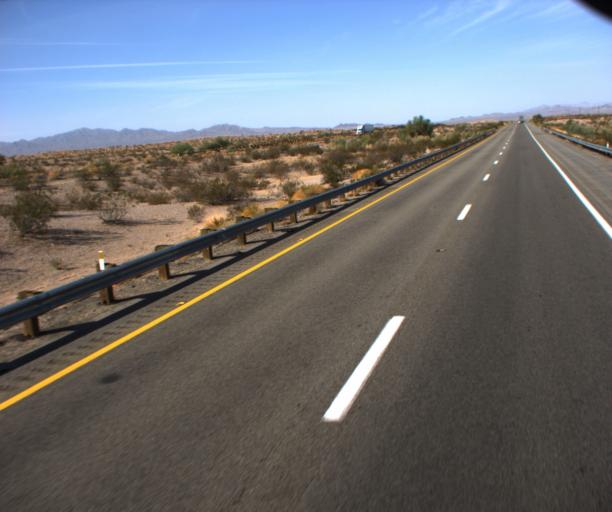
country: US
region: Arizona
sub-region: Mohave County
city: Desert Hills
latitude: 34.7722
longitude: -114.1928
